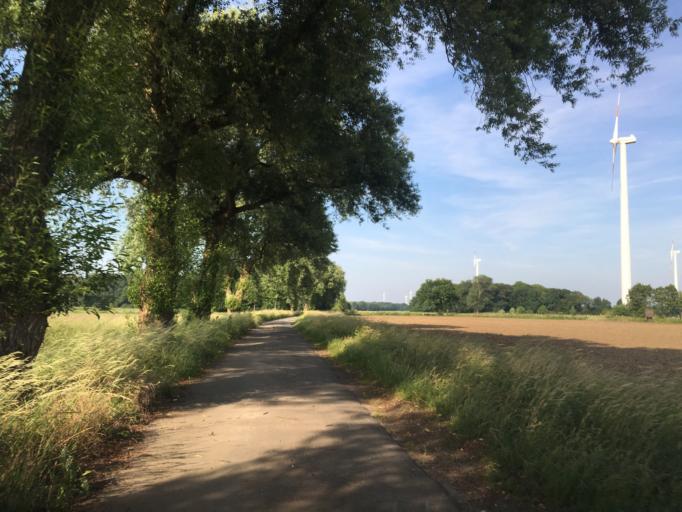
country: DE
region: North Rhine-Westphalia
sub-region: Regierungsbezirk Munster
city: Greven
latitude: 52.0407
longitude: 7.5592
